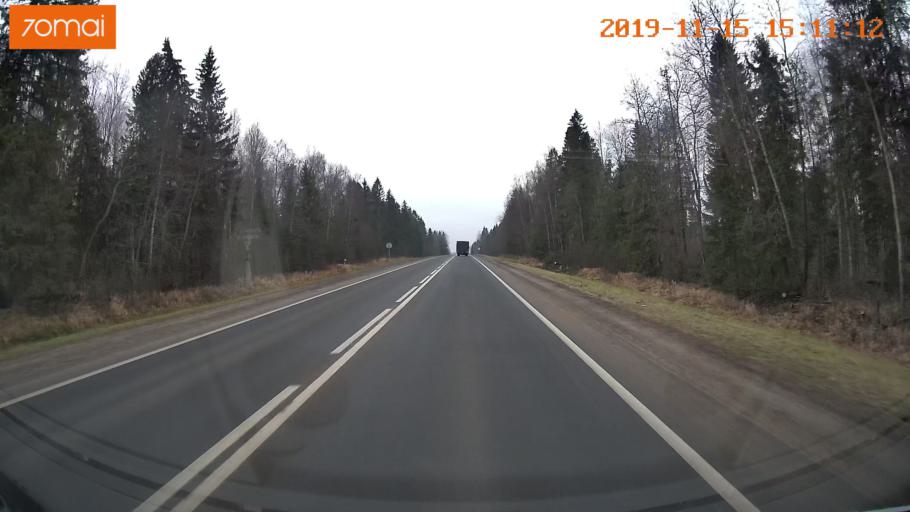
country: RU
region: Jaroslavl
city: Prechistoye
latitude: 58.3395
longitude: 40.2449
